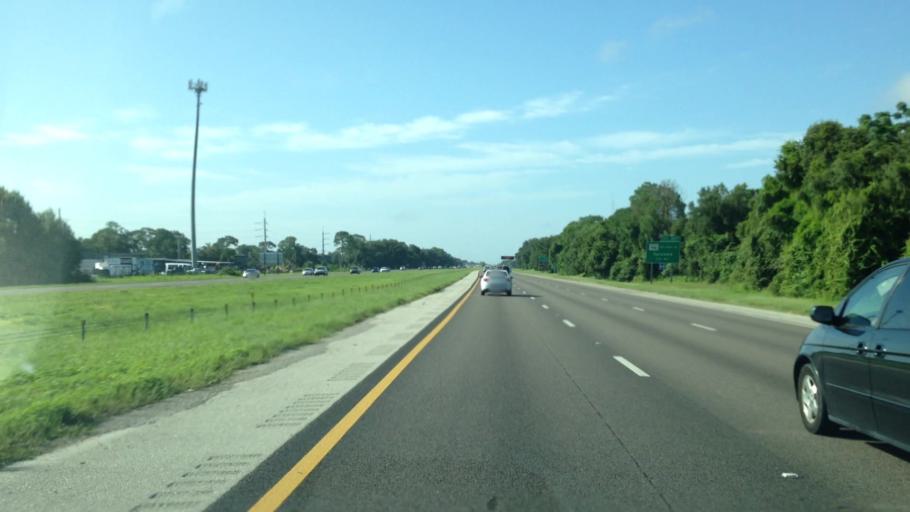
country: US
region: Florida
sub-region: Sarasota County
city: Fruitville
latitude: 27.3230
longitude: -82.4485
